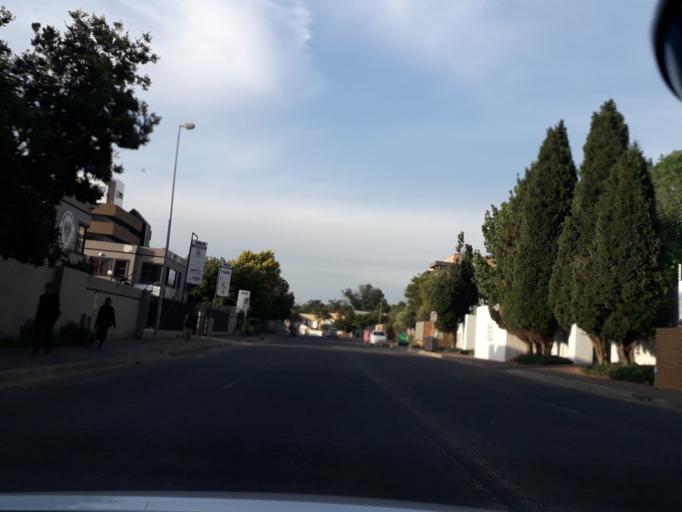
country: ZA
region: Gauteng
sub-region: City of Johannesburg Metropolitan Municipality
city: Johannesburg
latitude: -26.0888
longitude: 28.0050
